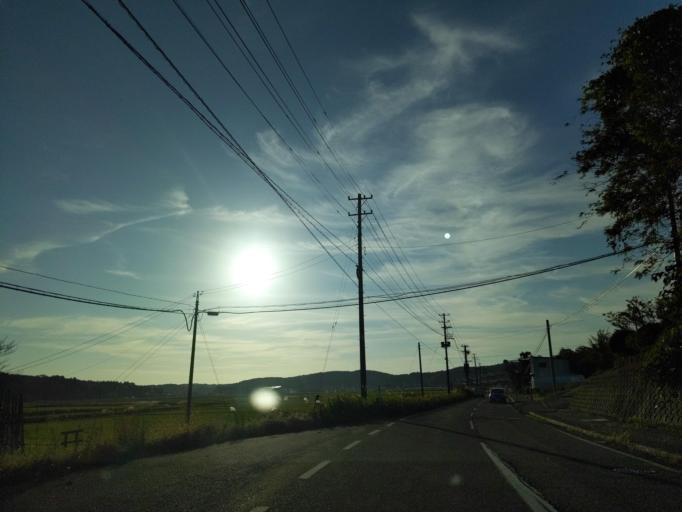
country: JP
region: Niigata
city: Nagaoka
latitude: 37.5778
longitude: 138.7599
